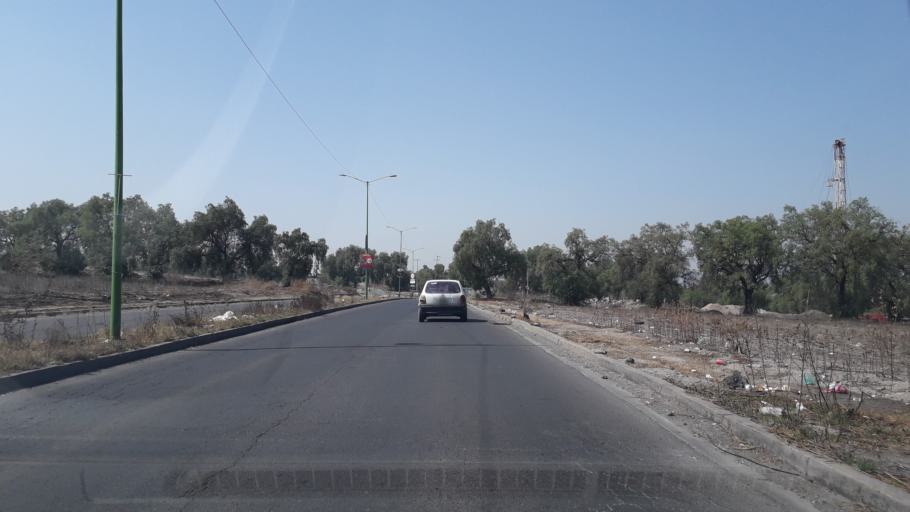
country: MX
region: Mexico
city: Santo Tomas Chiconautla
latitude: 19.6575
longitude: -99.0129
